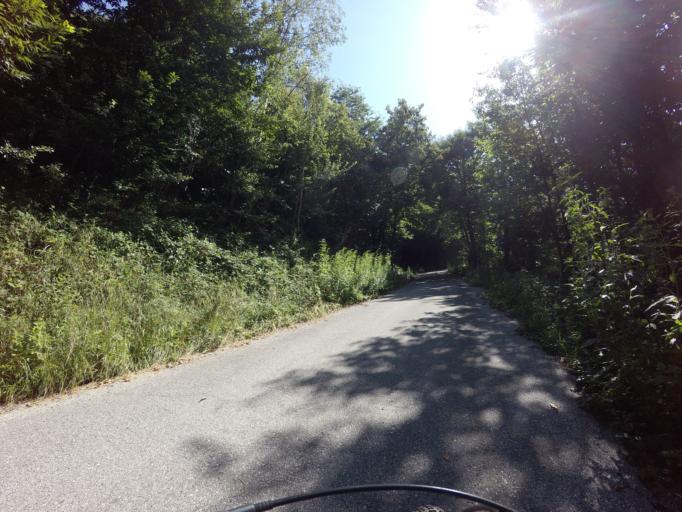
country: IT
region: Piedmont
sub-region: Provincia di Cuneo
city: Chiusa di Pesio
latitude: 44.2822
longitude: 7.6761
